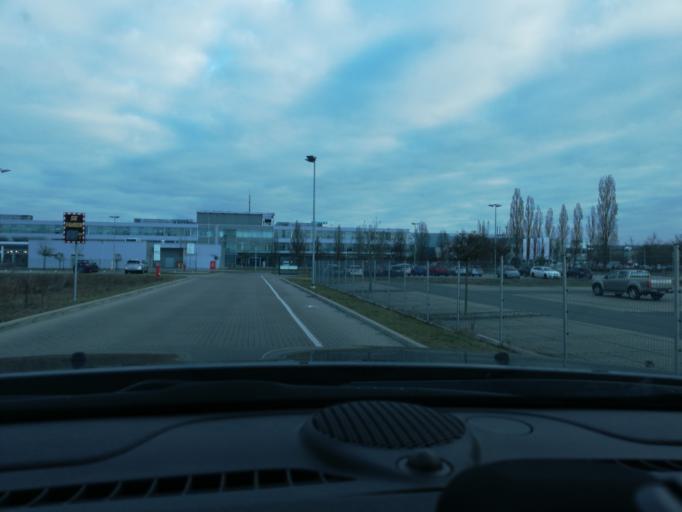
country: DE
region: Bavaria
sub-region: Upper Franconia
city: Forchheim
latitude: 49.7010
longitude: 11.0576
